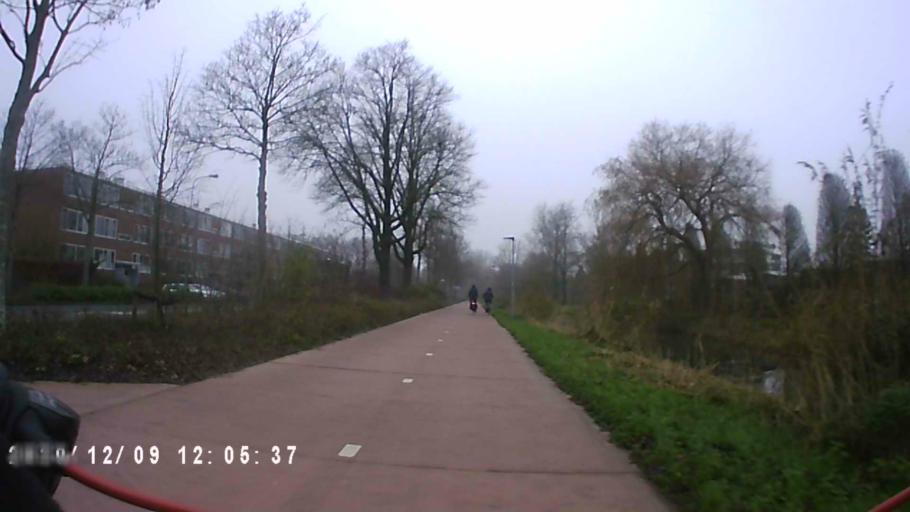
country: NL
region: Groningen
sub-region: Gemeente Haren
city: Haren
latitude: 53.1959
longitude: 6.5941
